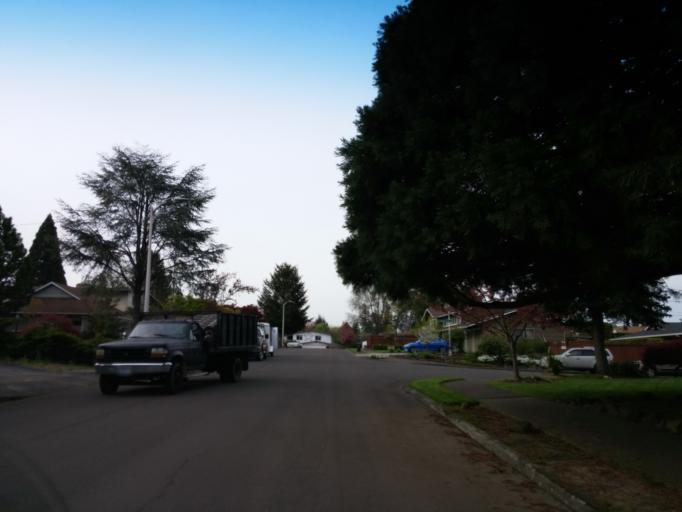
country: US
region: Oregon
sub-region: Washington County
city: Cedar Hills
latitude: 45.5080
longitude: -122.8120
